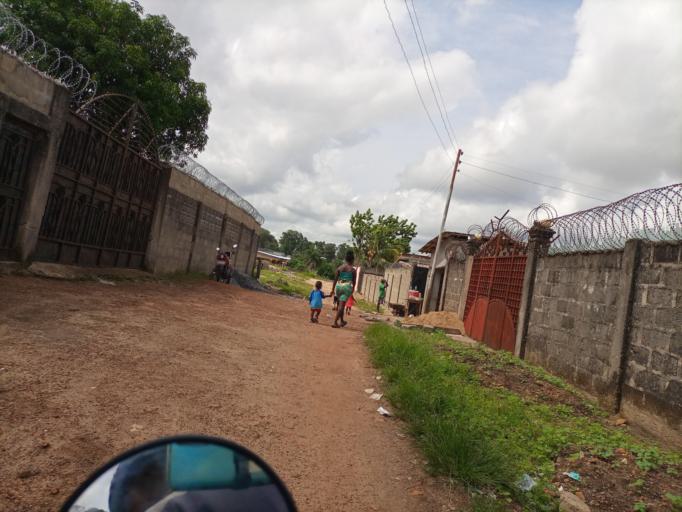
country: SL
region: Southern Province
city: Bo
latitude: 7.9731
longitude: -11.7578
